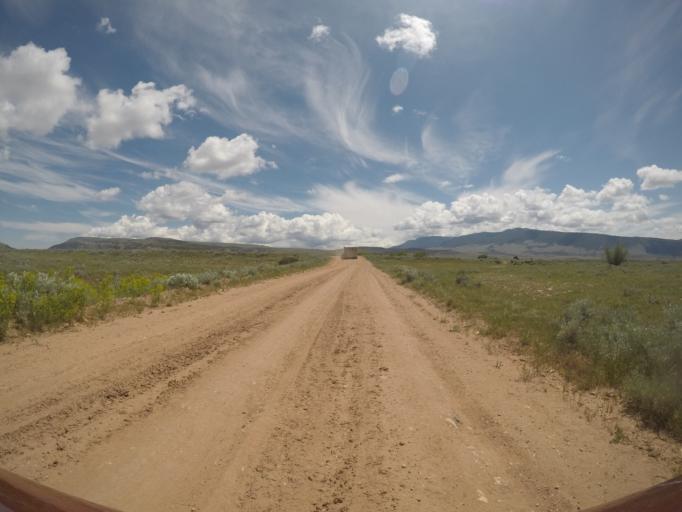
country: US
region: Montana
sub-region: Yellowstone County
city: Laurel
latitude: 45.2405
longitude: -108.6725
